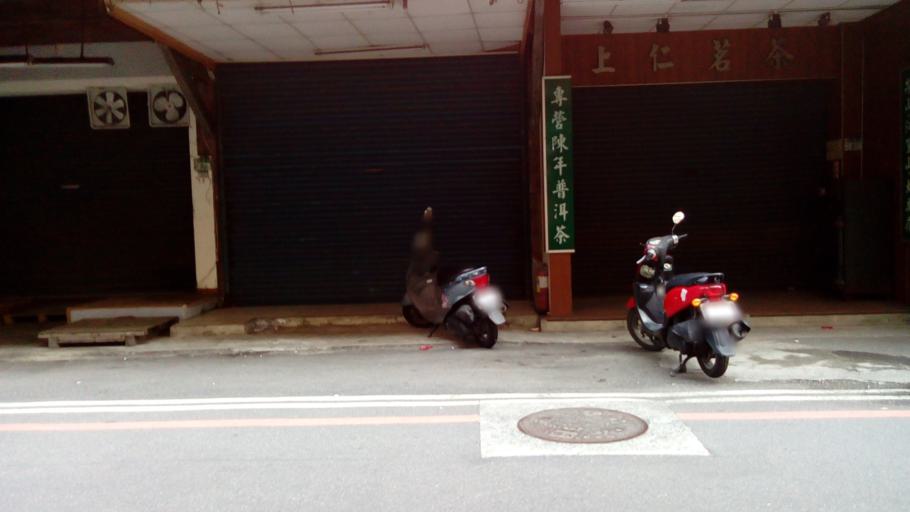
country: TW
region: Taipei
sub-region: Taipei
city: Banqiao
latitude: 24.9875
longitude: 121.5119
